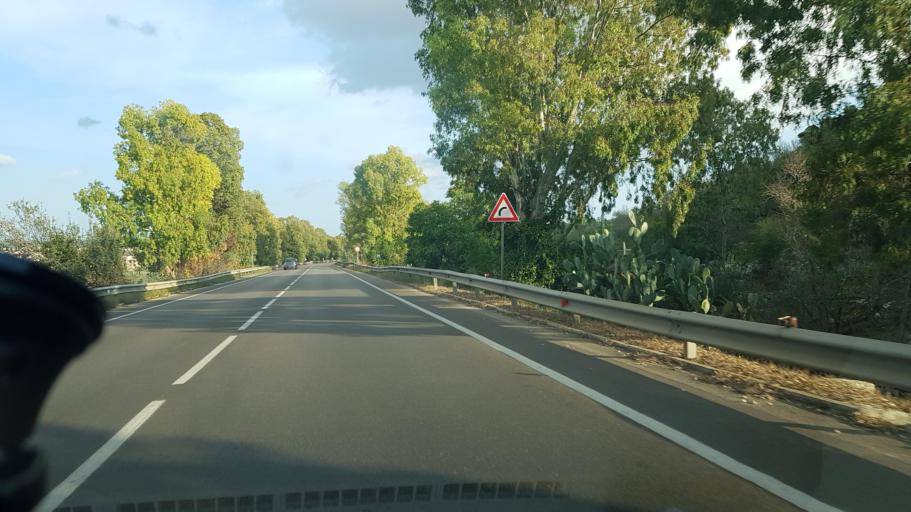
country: IT
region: Apulia
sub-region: Provincia di Lecce
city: Acquarica del Capo
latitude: 39.9060
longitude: 18.2410
